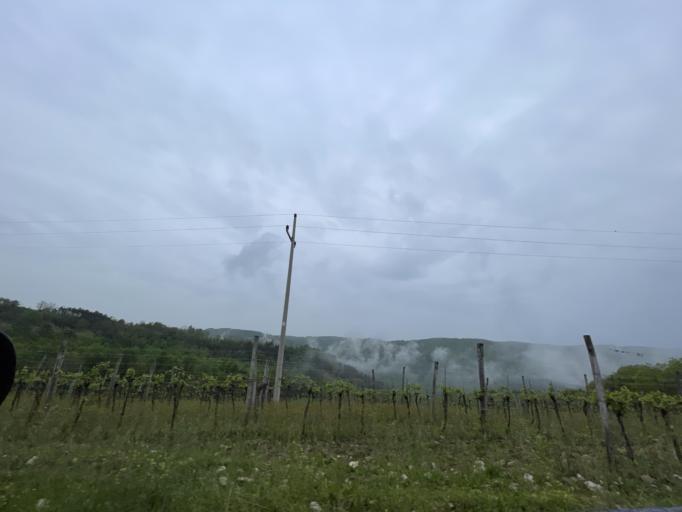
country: HR
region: Istarska
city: Karojba
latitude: 45.3286
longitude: 13.8054
